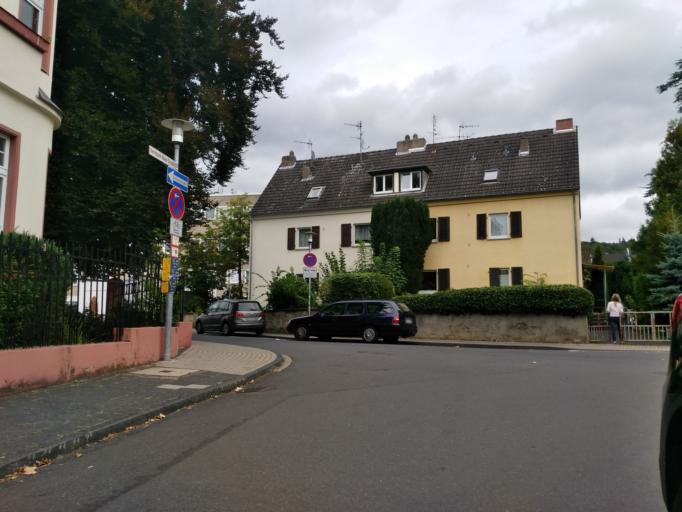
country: DE
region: North Rhine-Westphalia
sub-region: Regierungsbezirk Koln
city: Bad Honnef
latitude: 50.6468
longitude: 7.2259
